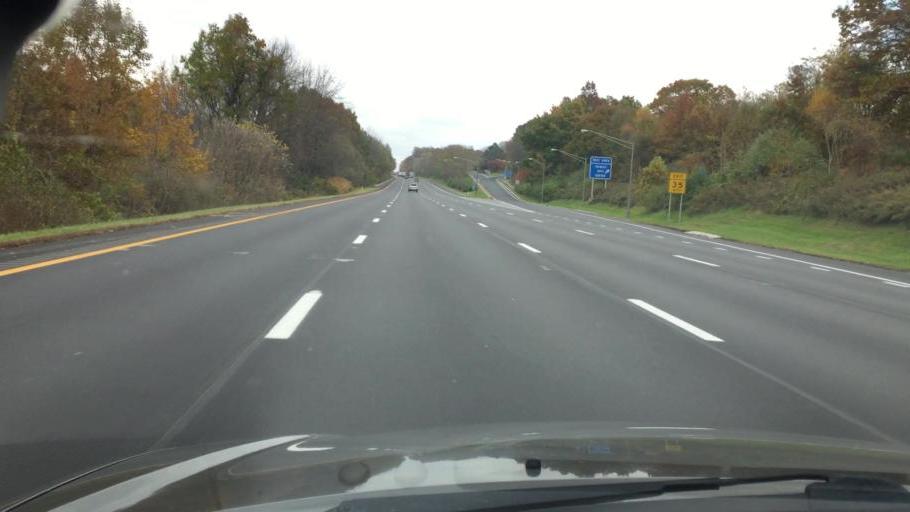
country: US
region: New Jersey
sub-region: Warren County
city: Belvidere
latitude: 40.9249
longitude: -75.0487
